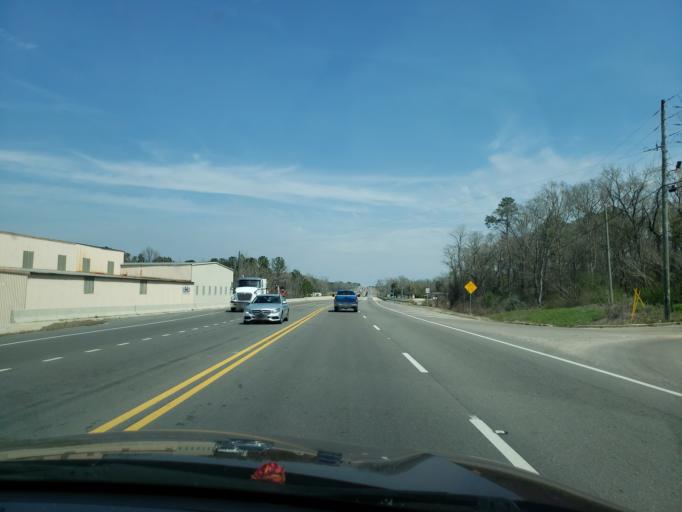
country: US
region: Alabama
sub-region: Elmore County
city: Elmore
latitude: 32.5330
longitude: -86.3232
